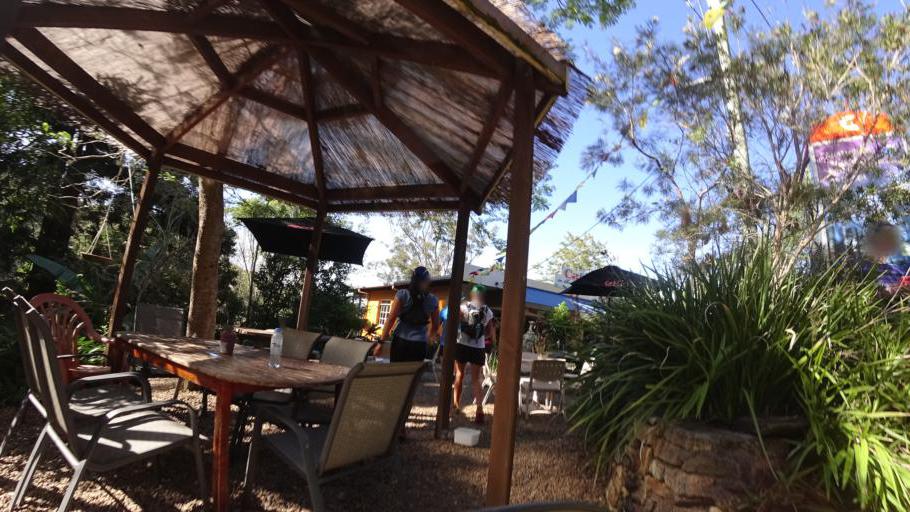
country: AU
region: Queensland
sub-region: Moreton Bay
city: Highvale
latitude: -27.3988
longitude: 152.7890
